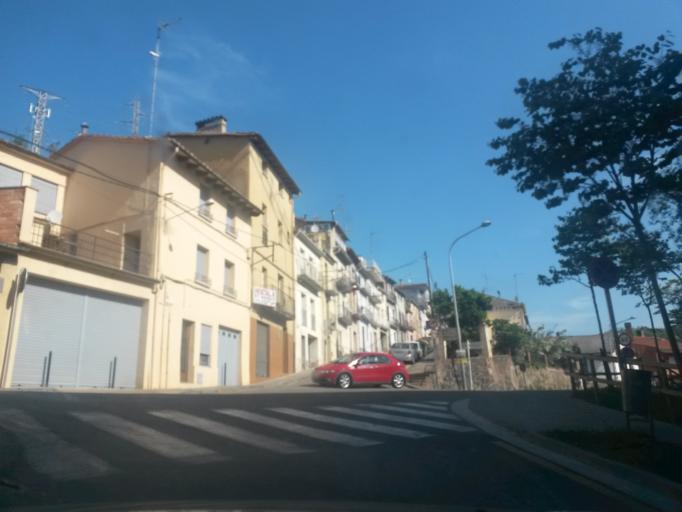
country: ES
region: Catalonia
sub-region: Provincia de Girona
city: MeteOlot
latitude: 42.1851
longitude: 2.4926
